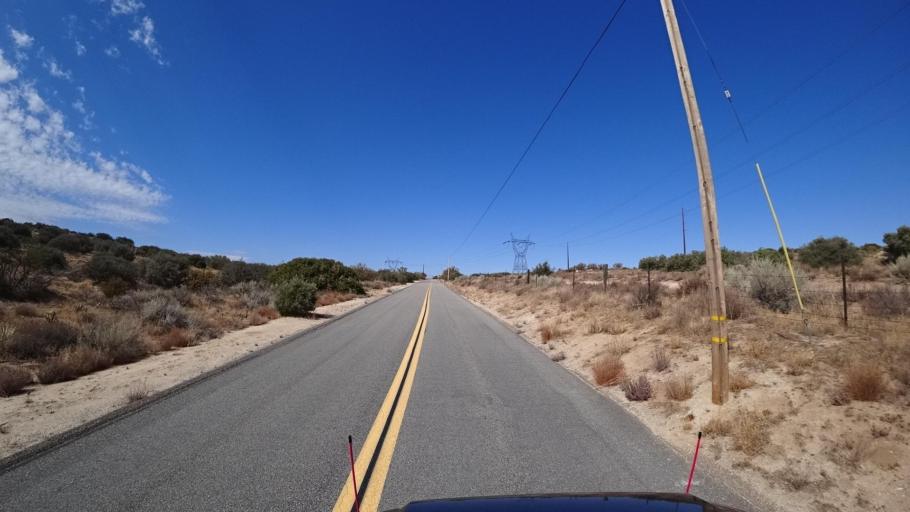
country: MX
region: Baja California
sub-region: Tecate
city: Cereso del Hongo
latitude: 32.6752
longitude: -116.2586
